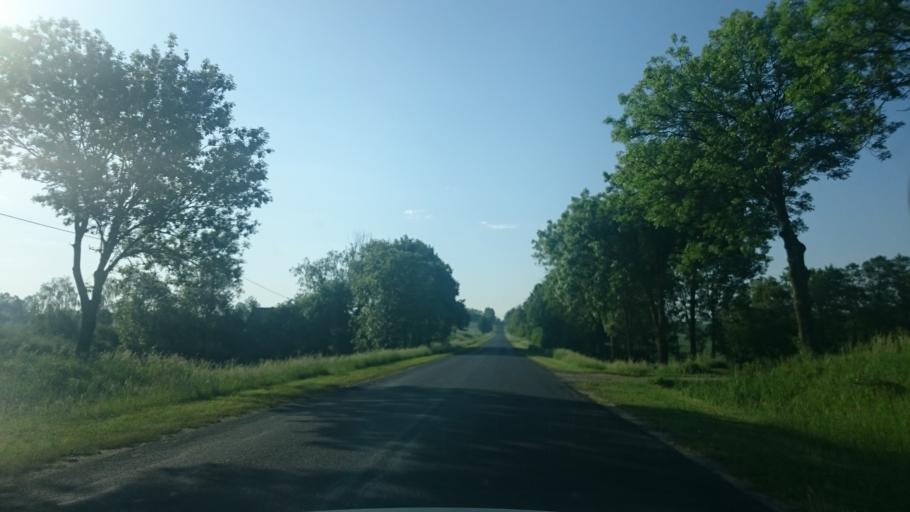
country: PL
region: Kujawsko-Pomorskie
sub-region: Powiat golubsko-dobrzynski
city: Zbojno
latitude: 53.0310
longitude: 19.1134
